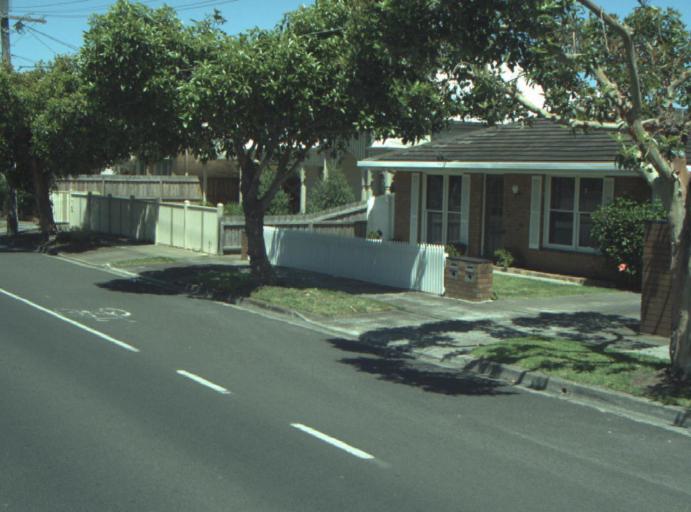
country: AU
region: Victoria
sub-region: Greater Geelong
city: Geelong West
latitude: -38.1325
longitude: 144.3536
